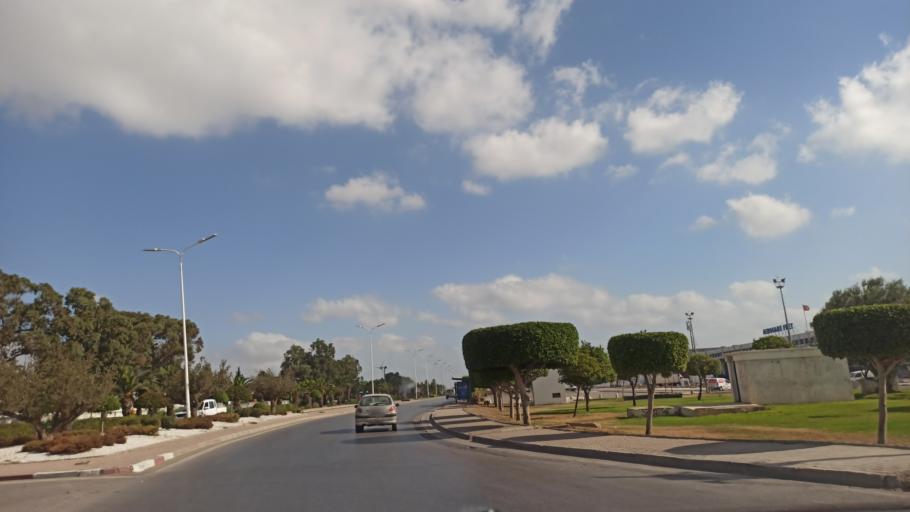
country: TN
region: Ariana
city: Ariana
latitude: 36.8354
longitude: 10.2130
